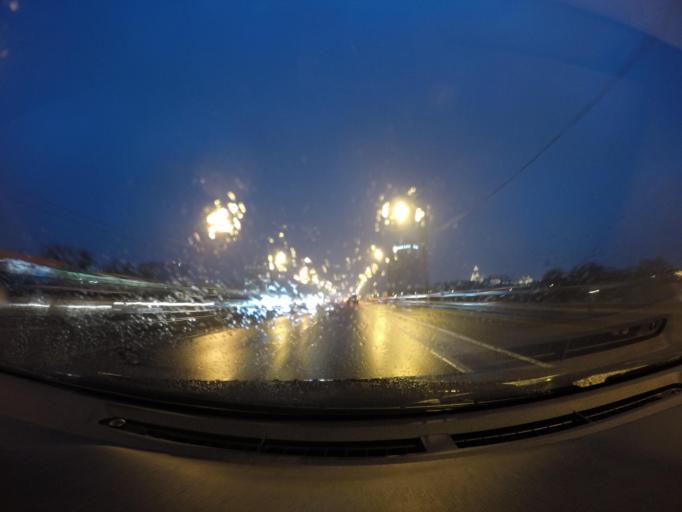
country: RU
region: Moskovskaya
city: Kozhukhovo
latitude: 55.6868
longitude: 37.6654
